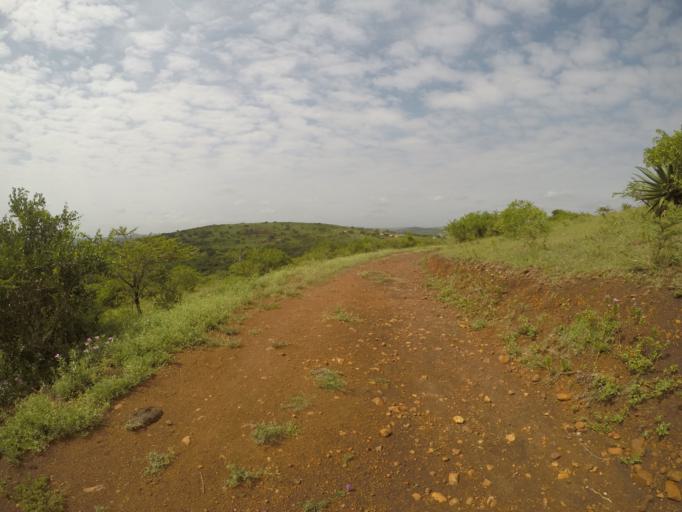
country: ZA
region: KwaZulu-Natal
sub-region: uThungulu District Municipality
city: Empangeni
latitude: -28.6181
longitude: 31.8991
